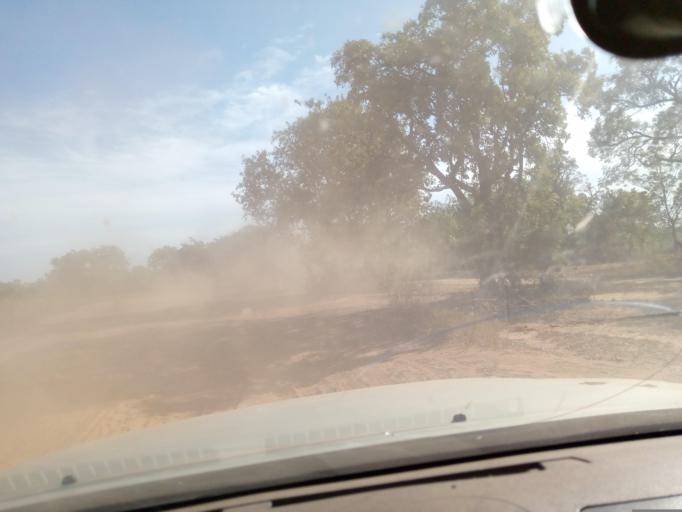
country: ML
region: Sikasso
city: Sikasso
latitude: 11.4747
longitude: -5.3320
